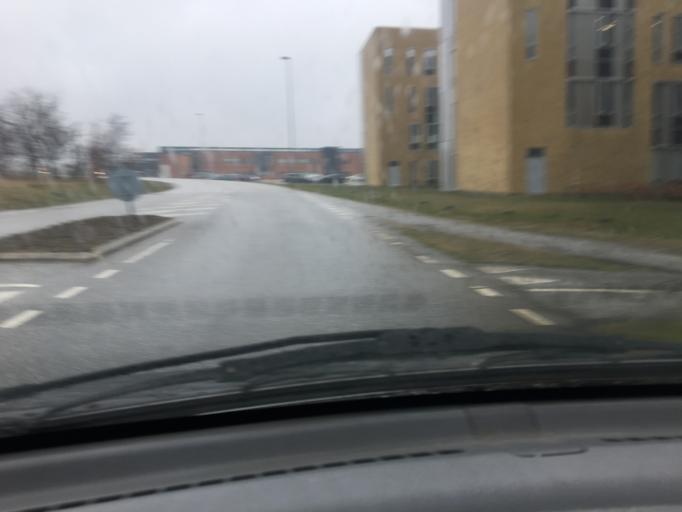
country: DK
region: North Denmark
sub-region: Alborg Kommune
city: Gistrup
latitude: 57.0109
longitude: 9.9944
